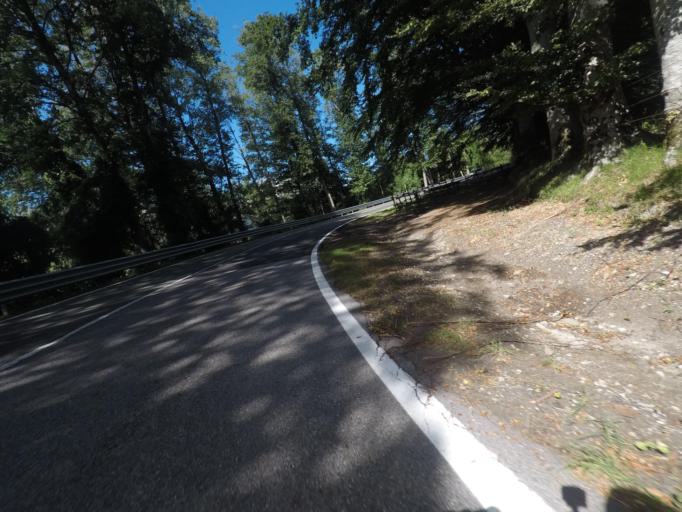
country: IT
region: Tuscany
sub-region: Provincia di Massa-Carrara
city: Comano
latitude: 44.2790
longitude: 10.1855
